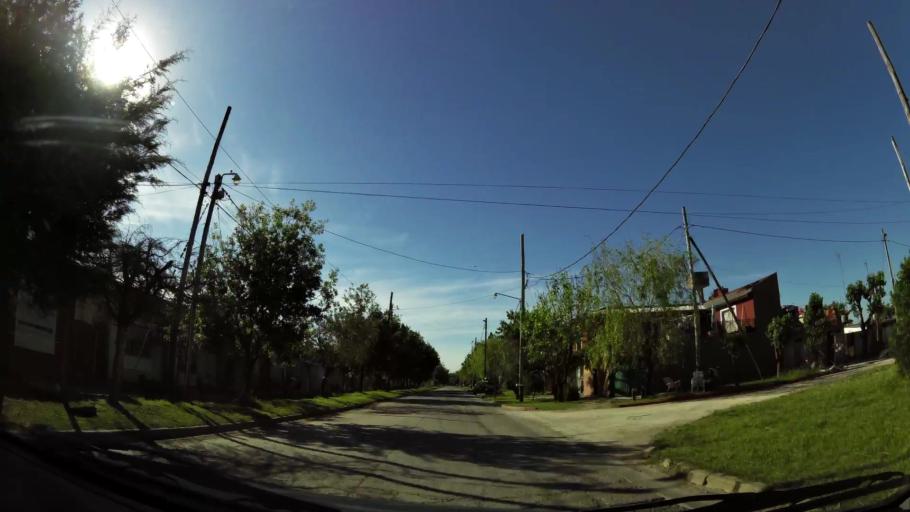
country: AR
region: Buenos Aires
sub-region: Partido de Almirante Brown
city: Adrogue
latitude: -34.8292
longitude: -58.3506
